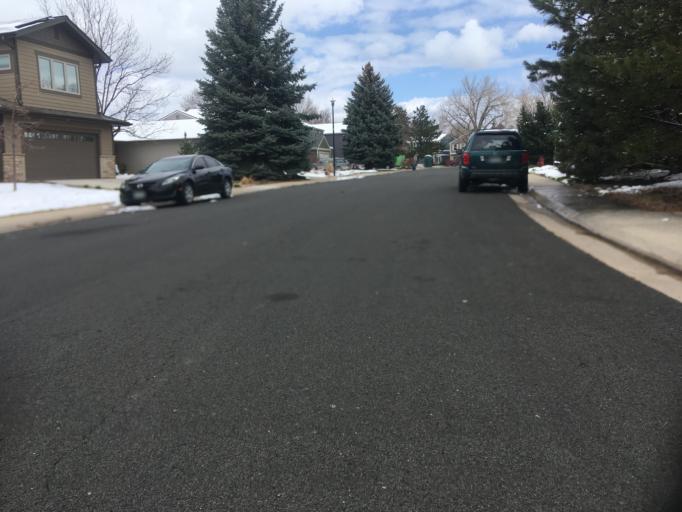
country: US
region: Colorado
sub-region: Boulder County
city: Louisville
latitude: 39.9713
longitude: -105.1402
